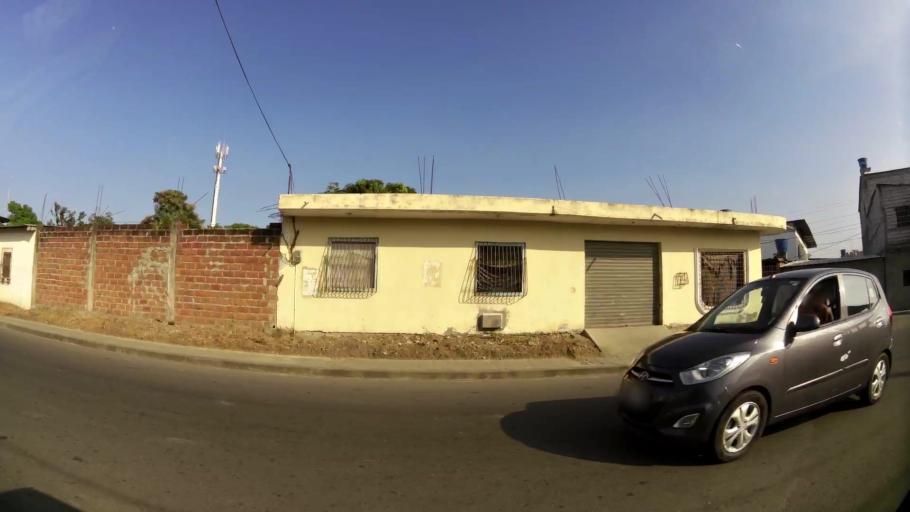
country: EC
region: Guayas
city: Eloy Alfaro
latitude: -2.1828
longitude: -79.8486
